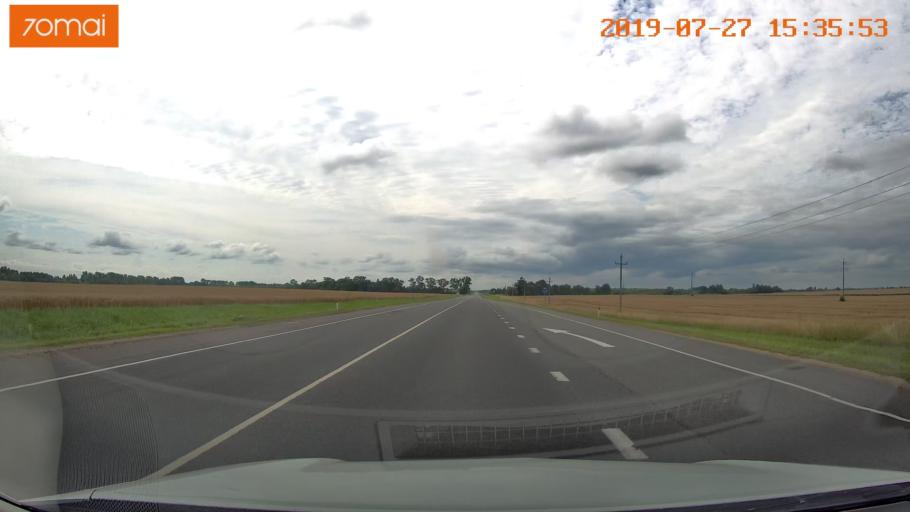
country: RU
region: Kaliningrad
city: Gusev
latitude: 54.6128
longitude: 22.3849
